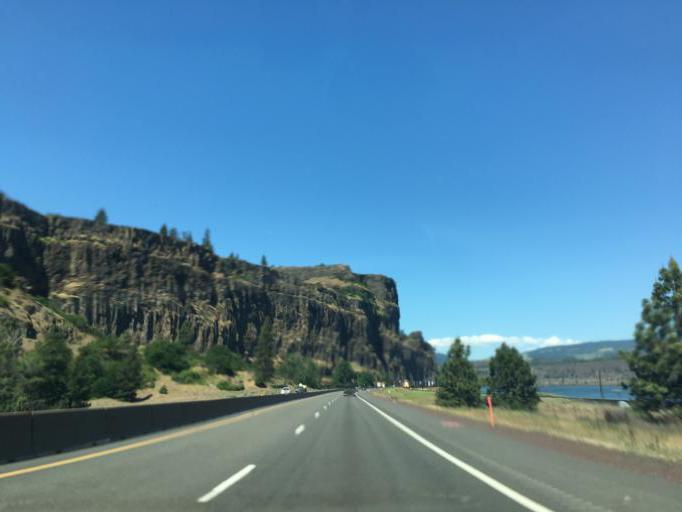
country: US
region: Oregon
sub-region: Wasco County
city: Chenoweth
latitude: 45.6844
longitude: -121.2940
